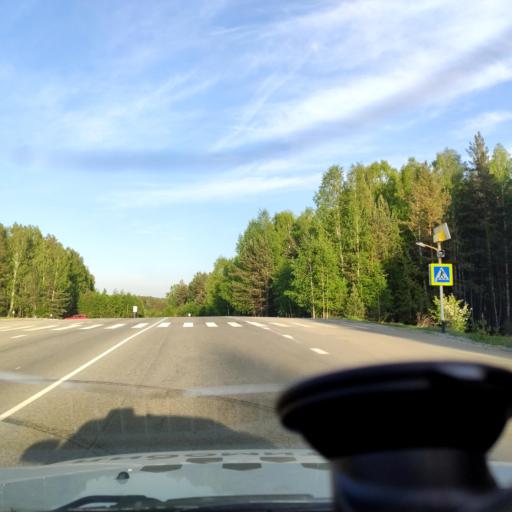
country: RU
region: Sverdlovsk
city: Talitsa
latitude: 56.8701
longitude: 60.0472
